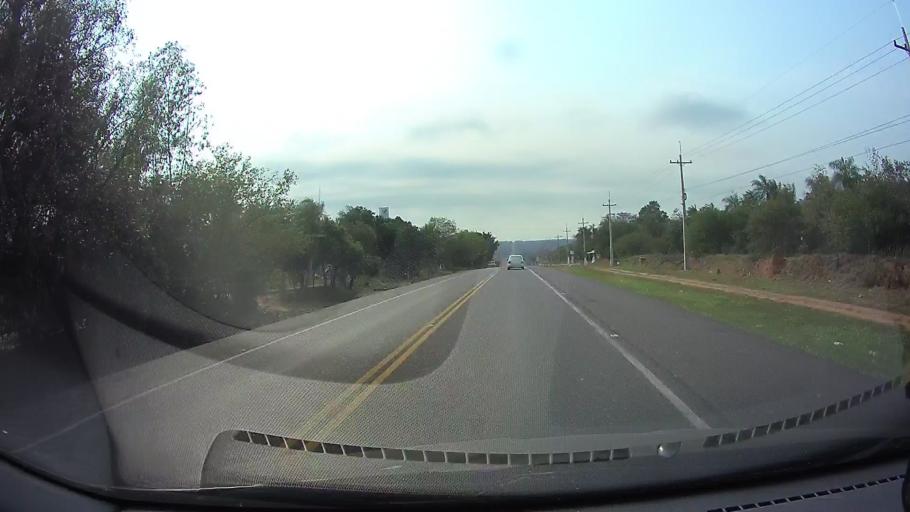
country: PY
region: Cordillera
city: Arroyos y Esteros
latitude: -25.0660
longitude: -57.2110
